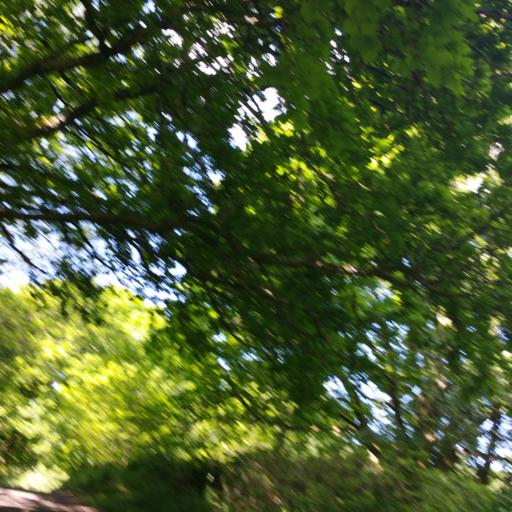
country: GB
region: Scotland
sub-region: East Dunbartonshire
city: Milngavie
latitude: 55.9497
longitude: -4.3223
